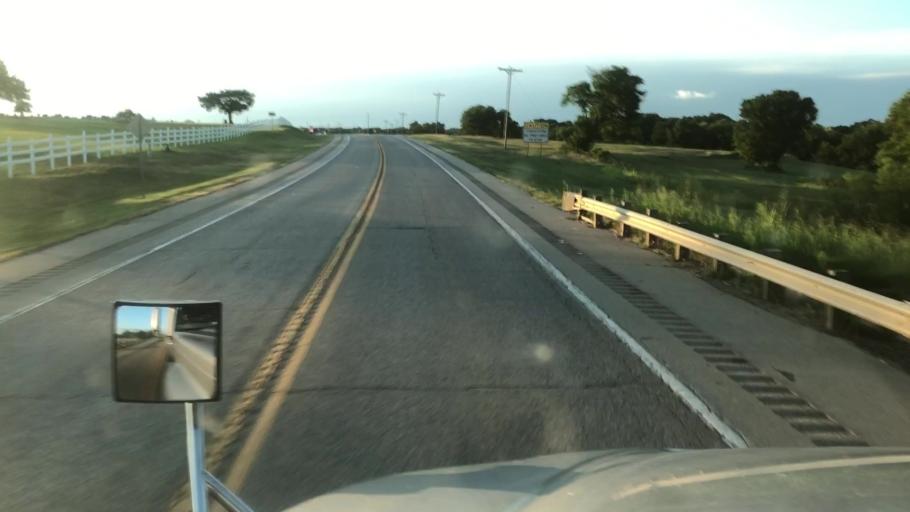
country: US
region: Oklahoma
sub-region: Osage County
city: McCord
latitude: 36.4840
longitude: -97.0695
